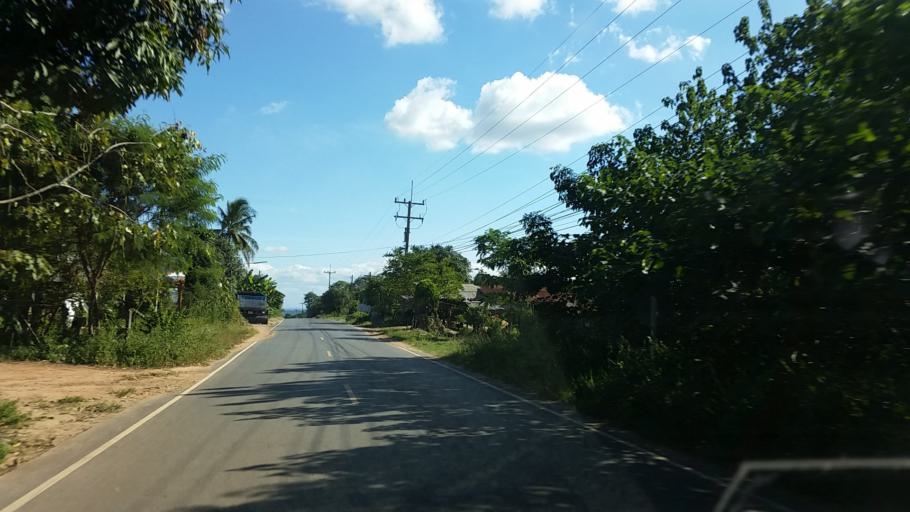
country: TH
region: Chaiyaphum
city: Thep Sathit
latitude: 15.5440
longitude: 101.4132
